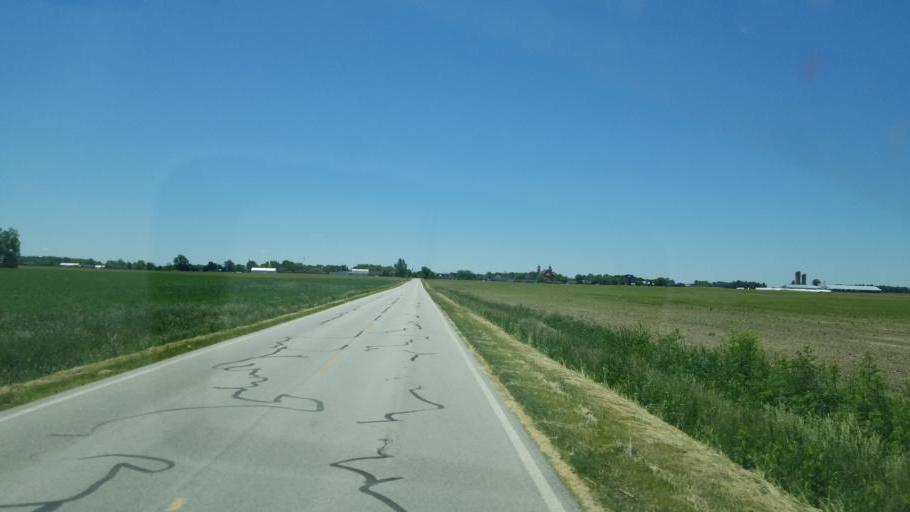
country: US
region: Ohio
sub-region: Mercer County
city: Saint Henry
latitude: 40.3631
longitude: -84.6433
